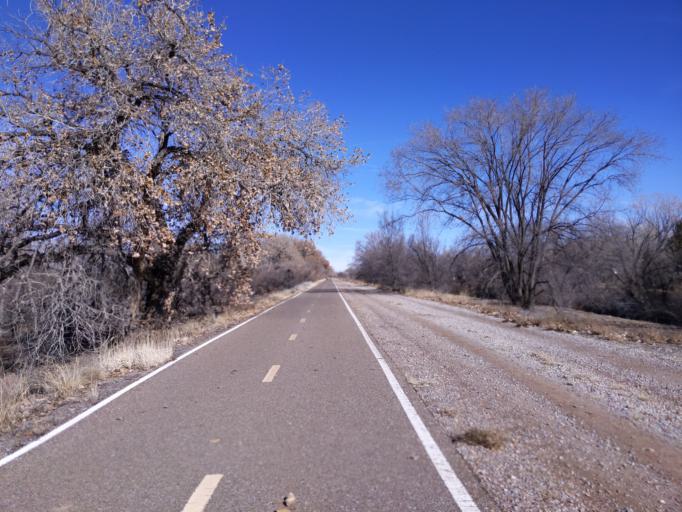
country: US
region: New Mexico
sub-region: Bernalillo County
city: Lee Acres
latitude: 35.1534
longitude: -106.6696
